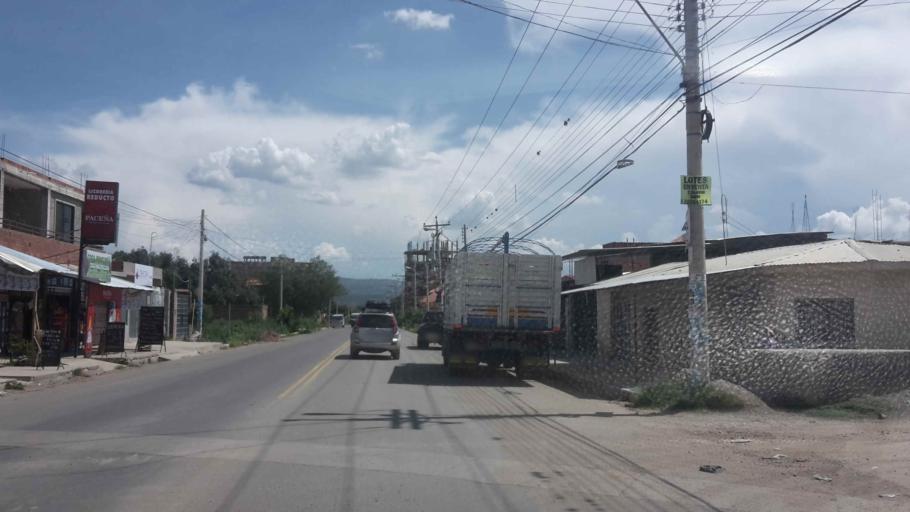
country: BO
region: Cochabamba
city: Cochabamba
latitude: -17.3763
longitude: -66.2340
